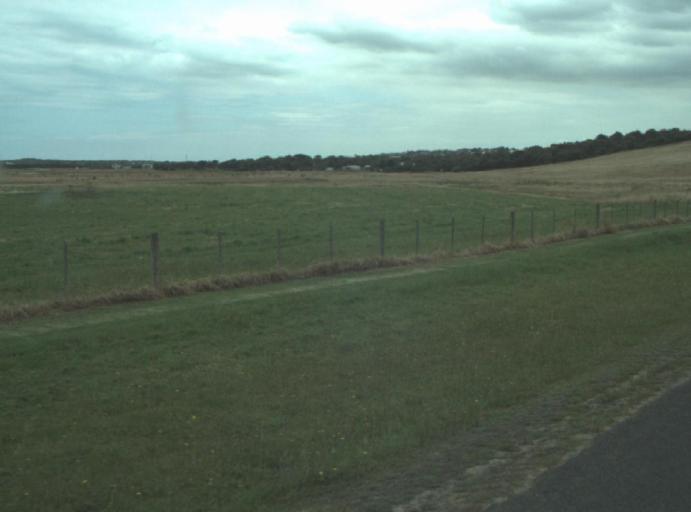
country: AU
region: Victoria
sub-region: Queenscliffe
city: Queenscliff
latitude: -38.2622
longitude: 144.5657
